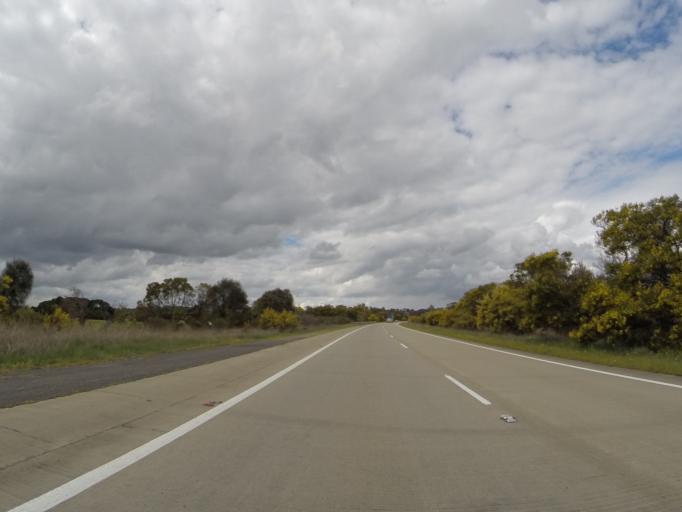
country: AU
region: New South Wales
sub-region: Goulburn Mulwaree
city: Goulburn
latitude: -34.8127
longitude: 149.4712
